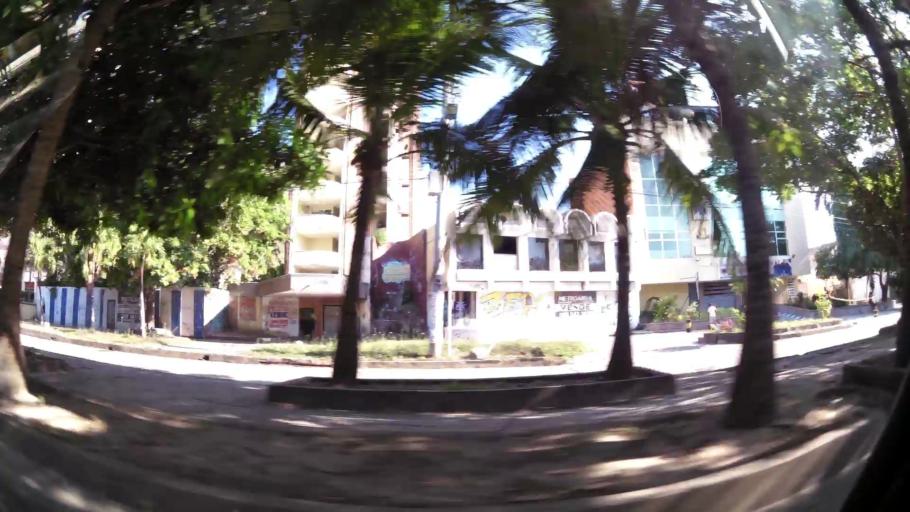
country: CO
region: Atlantico
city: Barranquilla
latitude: 10.9975
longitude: -74.7986
